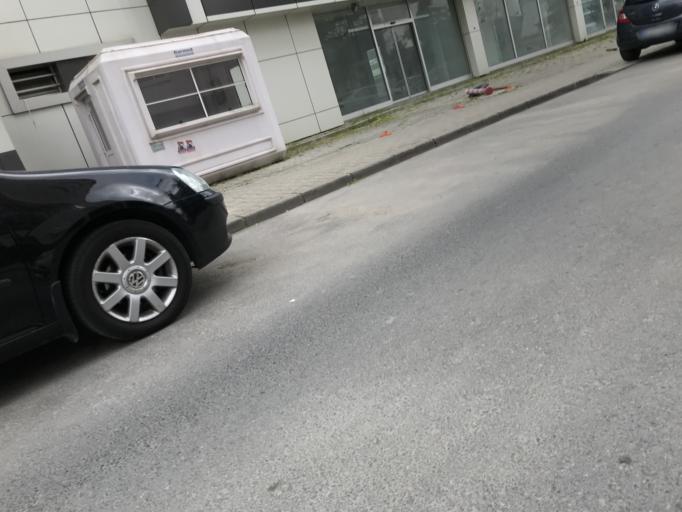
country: TR
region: Istanbul
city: Maltepe
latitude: 40.9392
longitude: 29.1361
